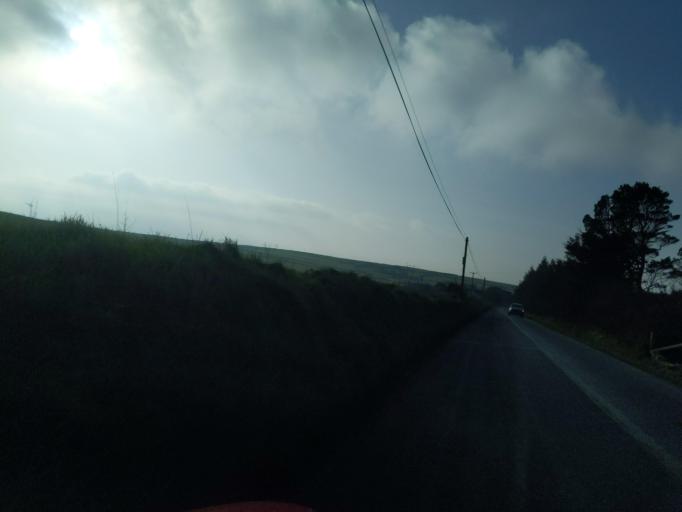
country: GB
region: England
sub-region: Cornwall
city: Camelford
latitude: 50.6454
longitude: -4.7017
